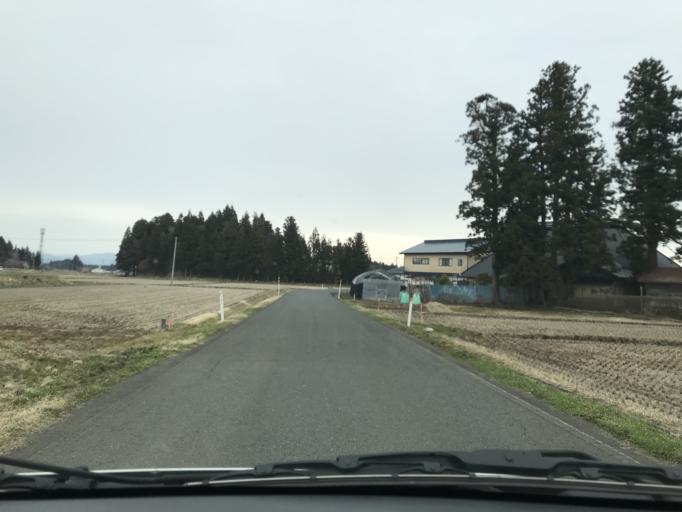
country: JP
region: Iwate
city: Mizusawa
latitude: 39.0924
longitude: 141.0803
